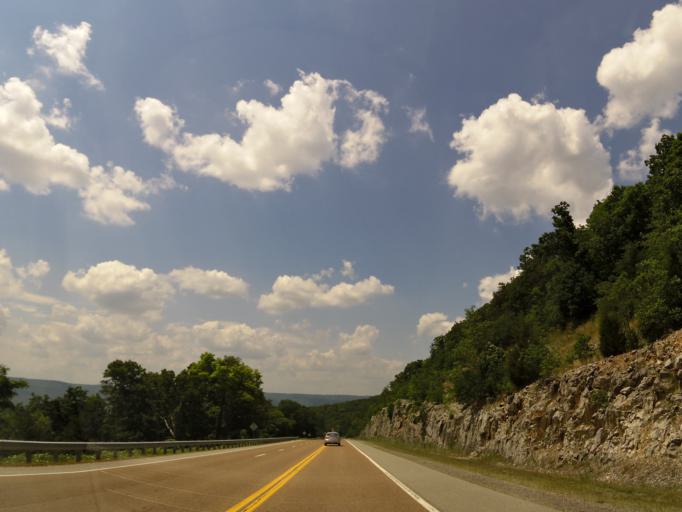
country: US
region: Tennessee
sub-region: Bledsoe County
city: Pikeville
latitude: 35.5763
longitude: -85.1572
